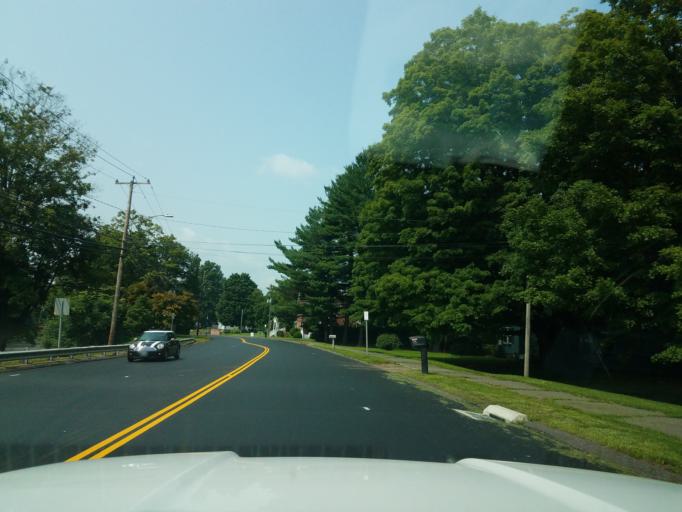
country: US
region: Connecticut
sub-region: Hartford County
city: Simsbury Center
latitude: 41.8707
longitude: -72.8086
